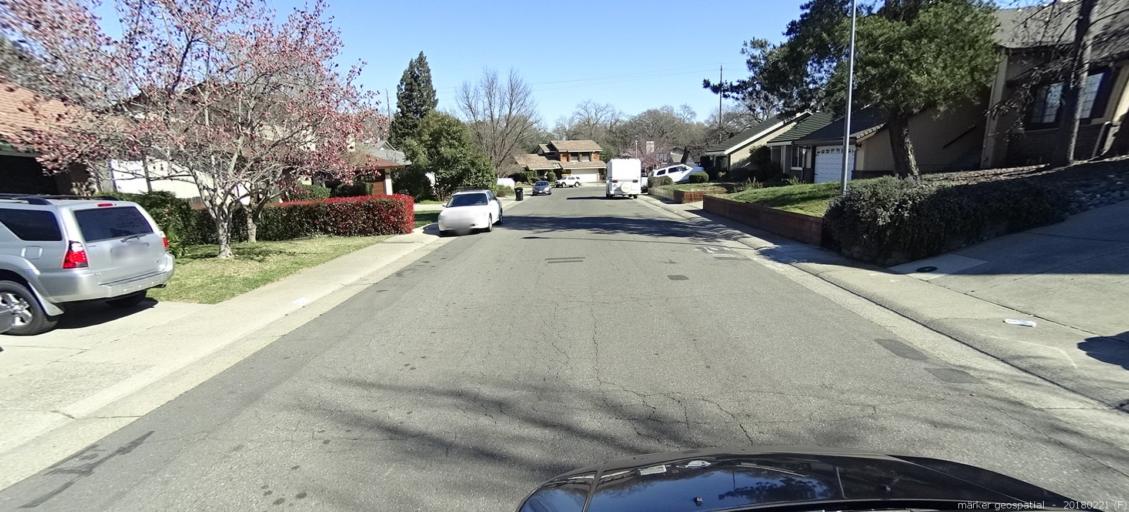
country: US
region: California
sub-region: Sacramento County
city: Orangevale
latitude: 38.6855
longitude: -121.2551
